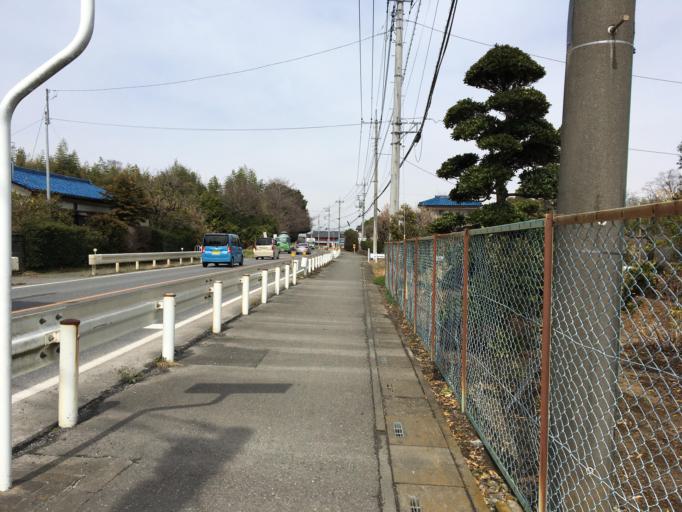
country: JP
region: Saitama
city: Yorii
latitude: 36.1440
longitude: 139.2089
